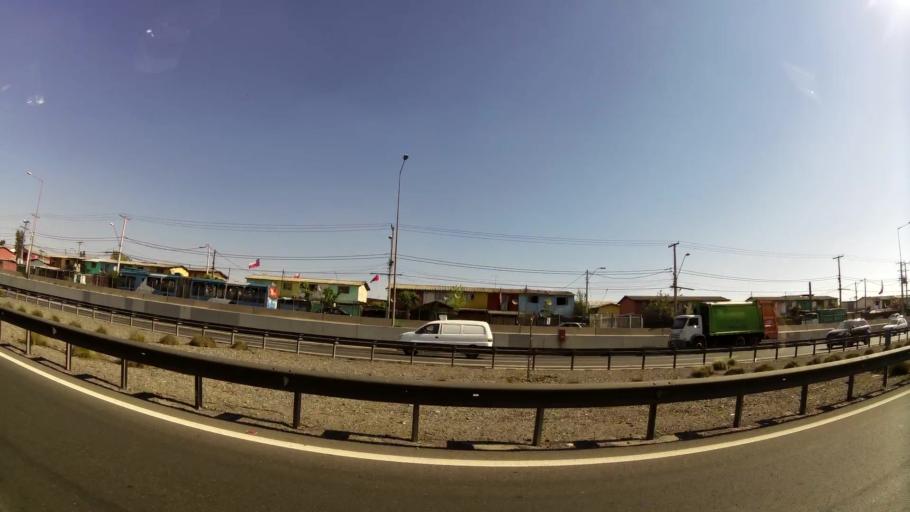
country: CL
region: Santiago Metropolitan
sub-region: Provincia de Maipo
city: San Bernardo
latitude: -33.5258
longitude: -70.6948
